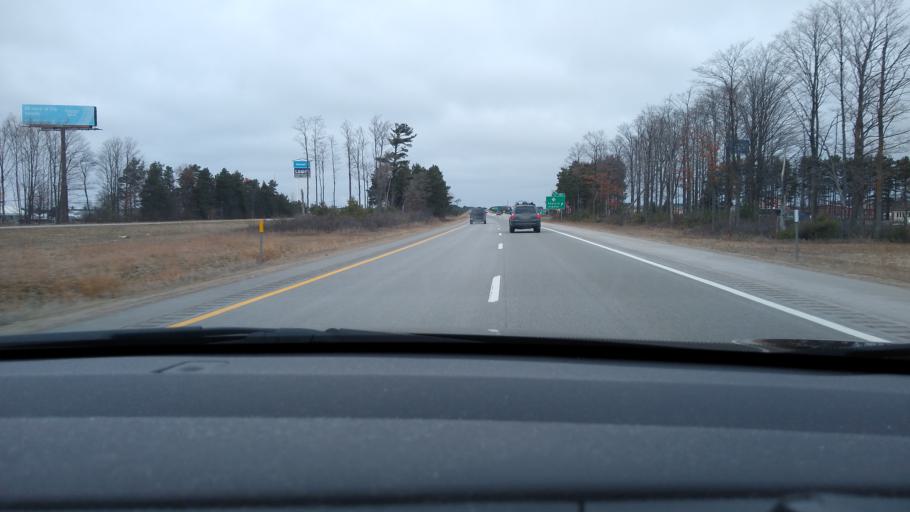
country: US
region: Michigan
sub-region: Otsego County
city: Gaylord
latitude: 45.0208
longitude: -84.6854
